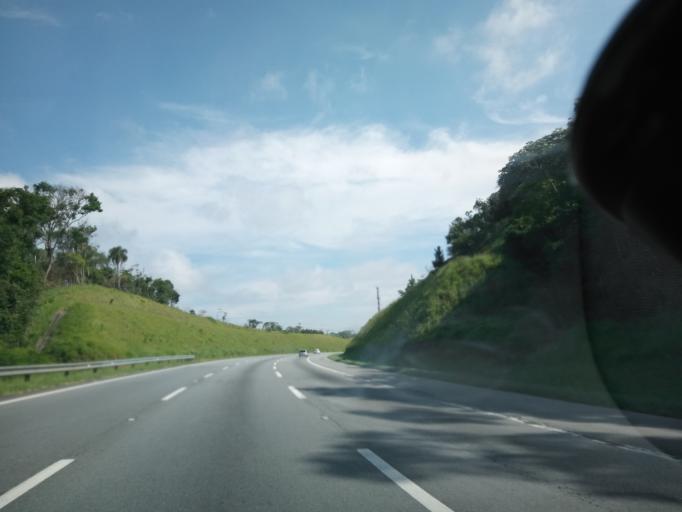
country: BR
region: Sao Paulo
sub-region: Embu
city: Embu
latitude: -23.6733
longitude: -46.8244
